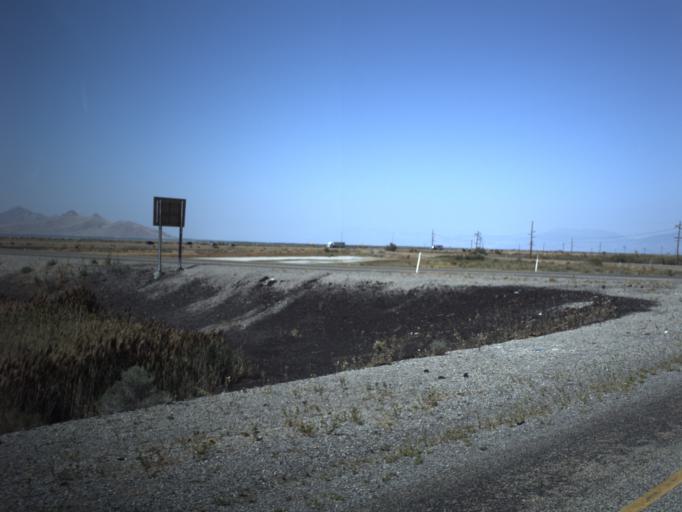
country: US
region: Utah
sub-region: Salt Lake County
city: Magna
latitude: 40.7430
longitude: -112.1809
